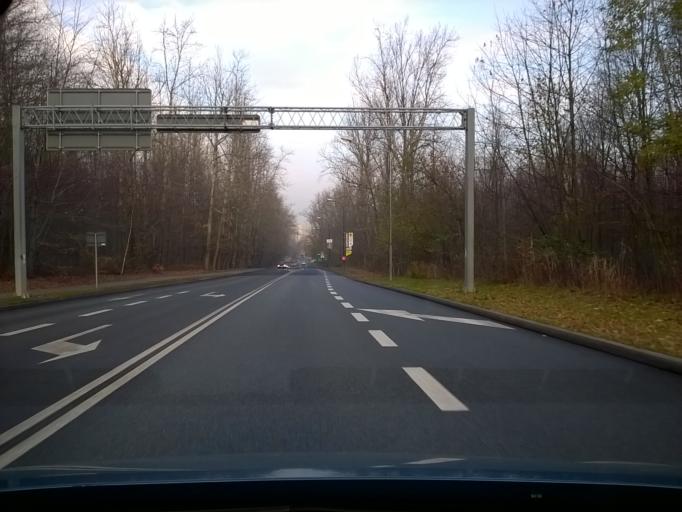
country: PL
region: Silesian Voivodeship
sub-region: Swietochlowice
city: Swietochlowice
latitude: 50.2556
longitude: 18.9366
